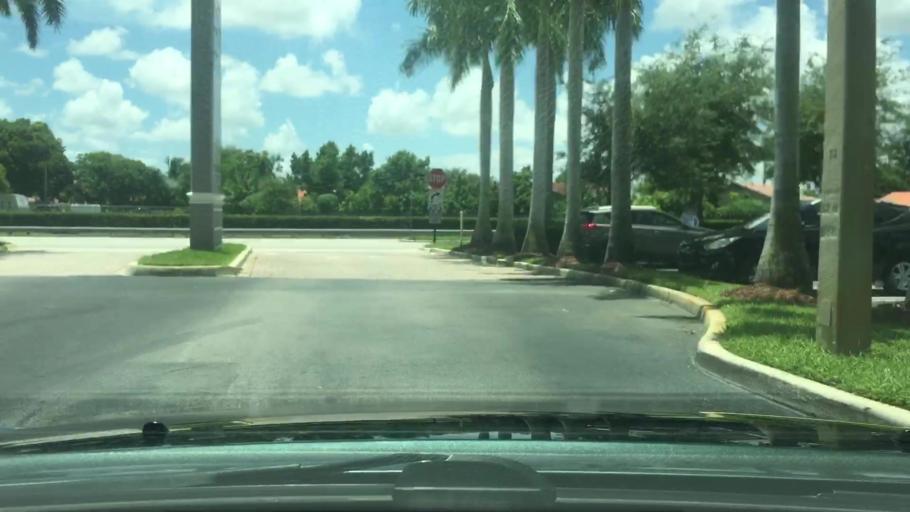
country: US
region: Florida
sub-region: Miami-Dade County
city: Kendall West
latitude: 25.7293
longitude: -80.4246
